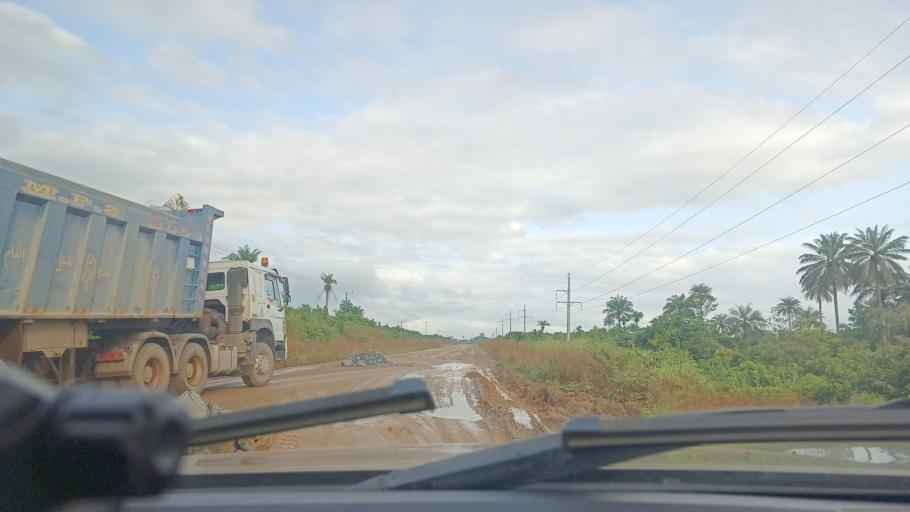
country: LR
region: Montserrado
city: Monrovia
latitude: 6.5748
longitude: -10.8831
